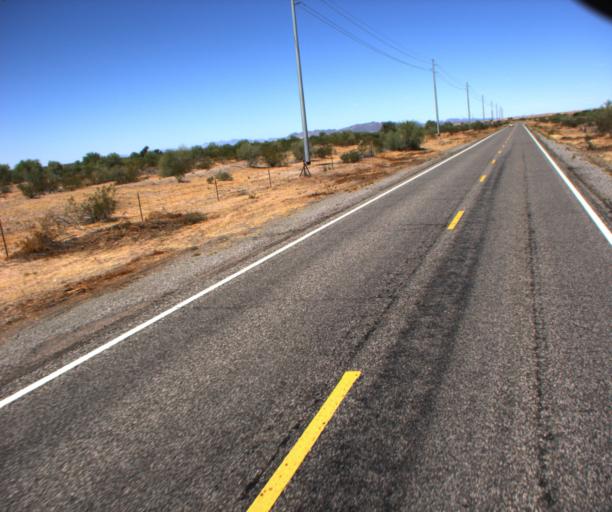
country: US
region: Arizona
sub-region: La Paz County
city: Cienega Springs
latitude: 33.9922
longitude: -114.0854
